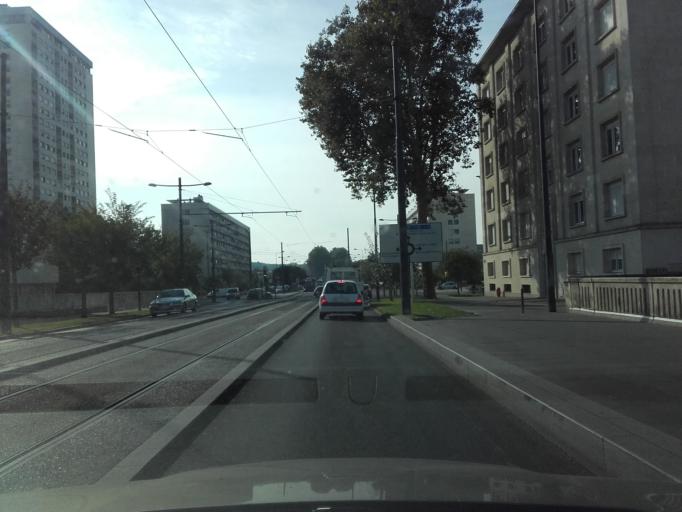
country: FR
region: Centre
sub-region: Departement d'Indre-et-Loire
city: Tours
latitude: 47.3749
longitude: 0.6950
